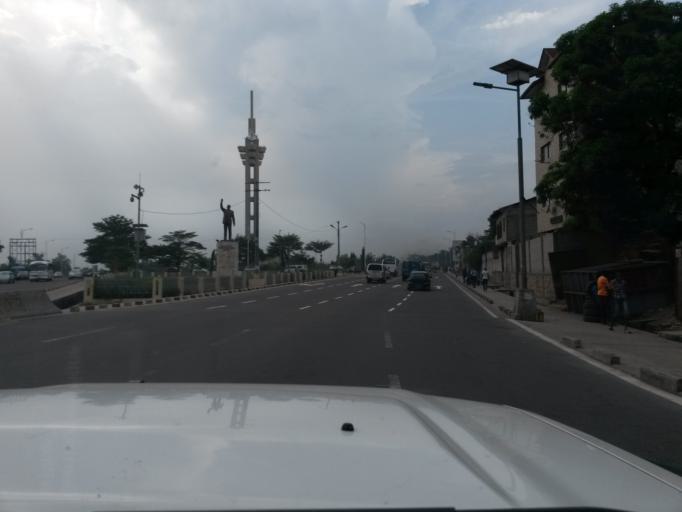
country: CD
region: Kinshasa
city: Masina
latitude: -4.3785
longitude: 15.3484
